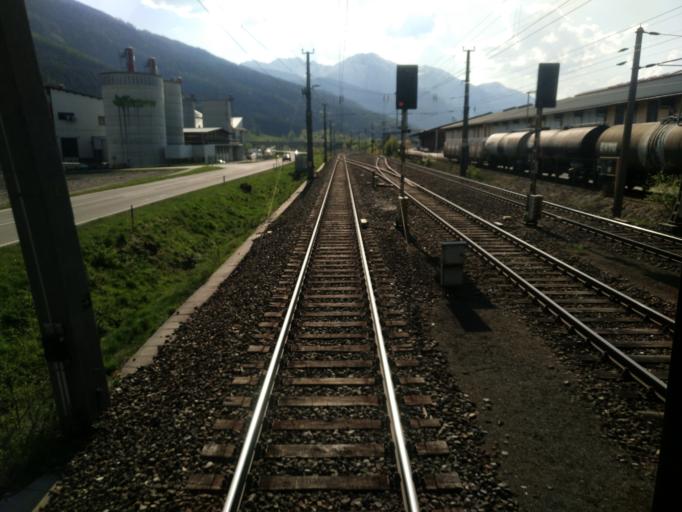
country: AT
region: Styria
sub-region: Politischer Bezirk Liezen
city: Treglwang
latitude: 47.4873
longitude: 14.5382
